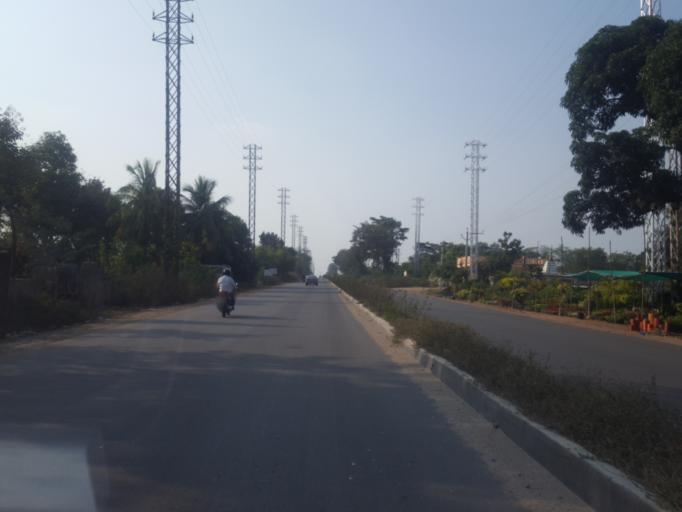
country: IN
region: Telangana
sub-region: Medak
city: Serilingampalle
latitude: 17.4129
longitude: 78.2663
